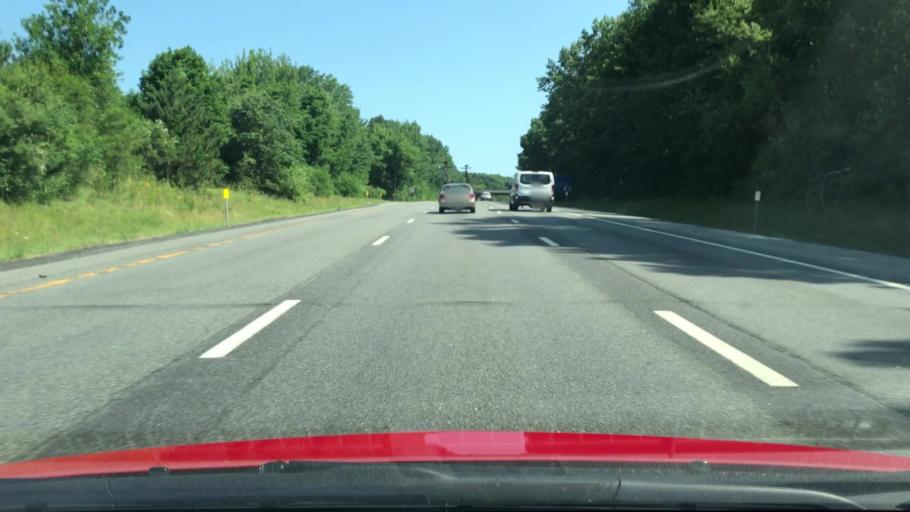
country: US
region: New York
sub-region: Saratoga County
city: Ballston Spa
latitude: 43.0094
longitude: -73.8004
